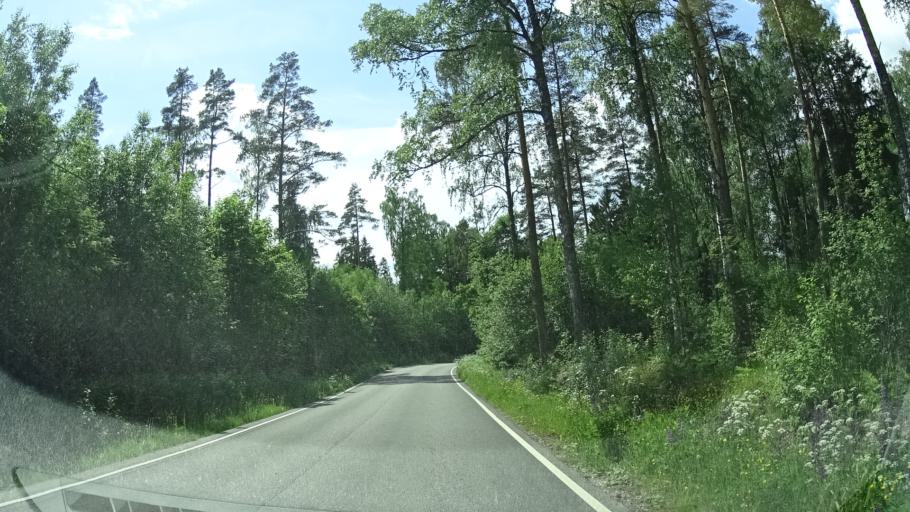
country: FI
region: Uusimaa
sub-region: Helsinki
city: Kirkkonummi
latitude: 60.2253
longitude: 24.3740
